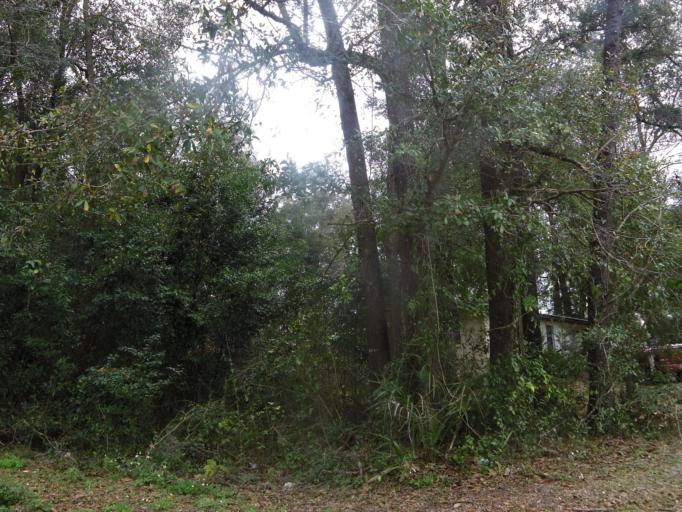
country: US
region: Florida
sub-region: Alachua County
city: High Springs
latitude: 29.8234
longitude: -82.6011
